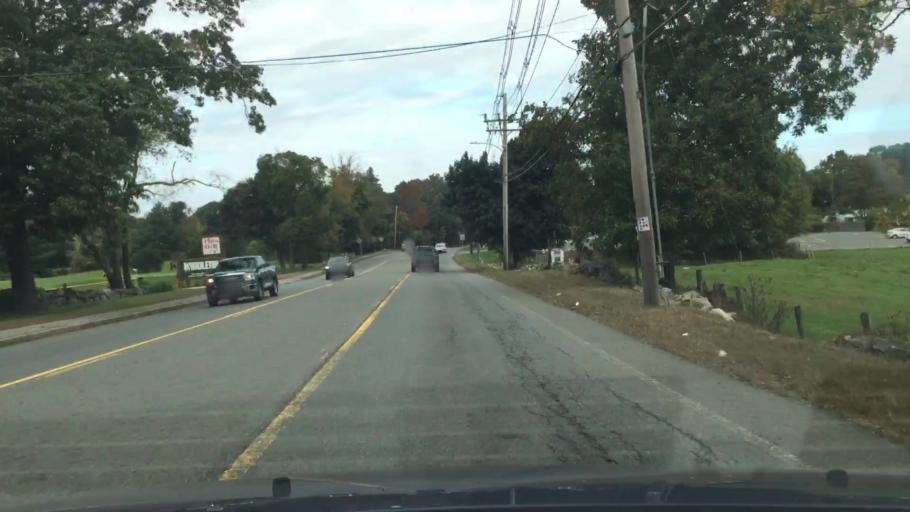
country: US
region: Massachusetts
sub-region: Essex County
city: Middleton
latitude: 42.5871
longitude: -71.0101
